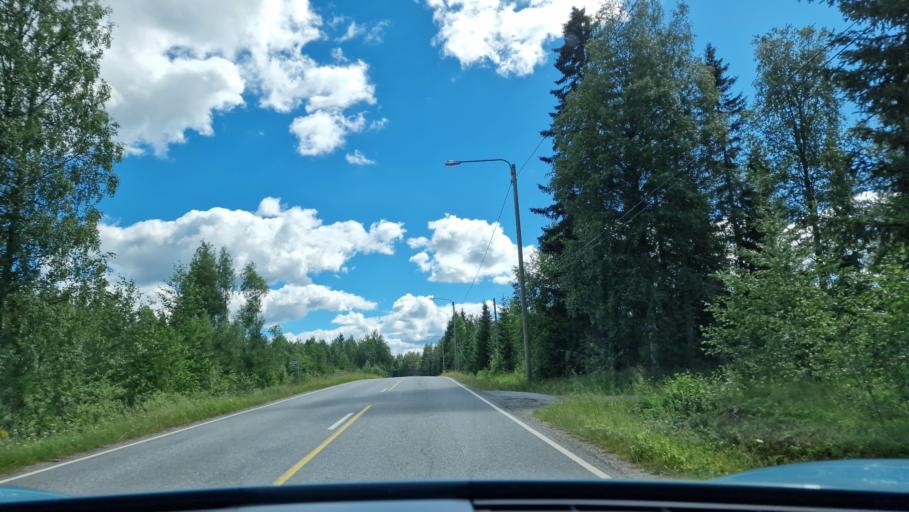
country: FI
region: Southern Ostrobothnia
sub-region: Jaerviseutu
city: Soini
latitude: 62.8382
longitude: 24.3300
